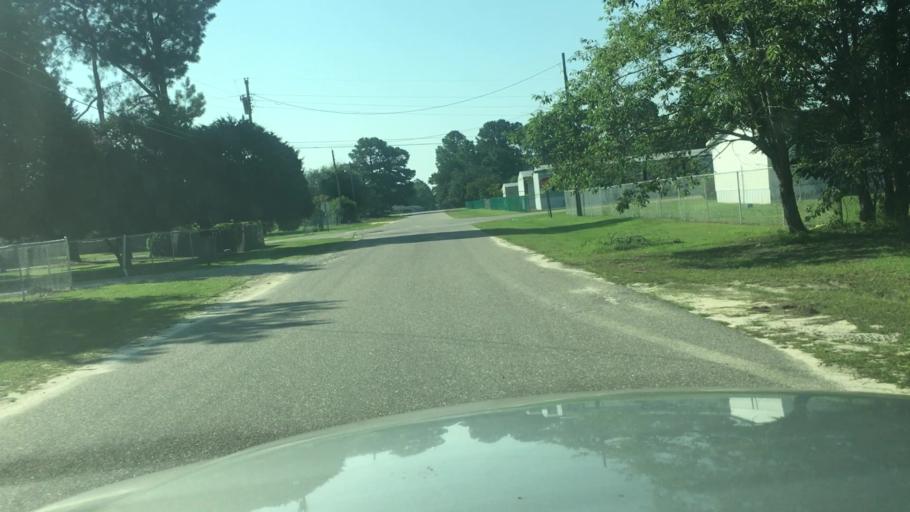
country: US
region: North Carolina
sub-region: Cumberland County
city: Spring Lake
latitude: 35.1495
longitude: -78.9163
